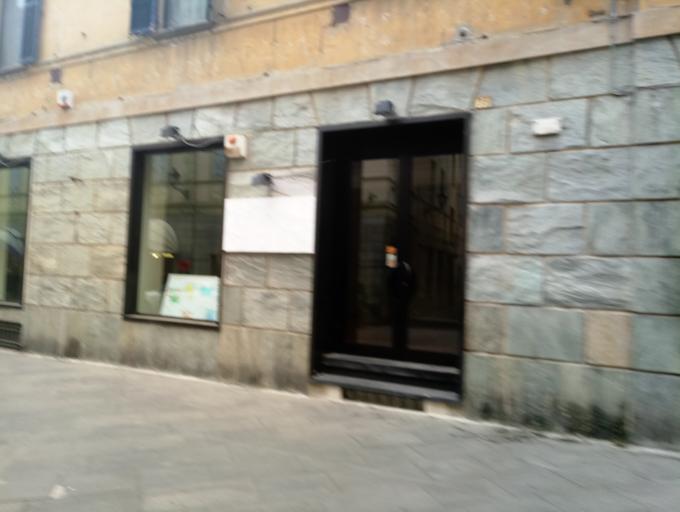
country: IT
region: Piedmont
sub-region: Provincia di Alessandria
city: Valenza
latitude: 45.0136
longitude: 8.6448
